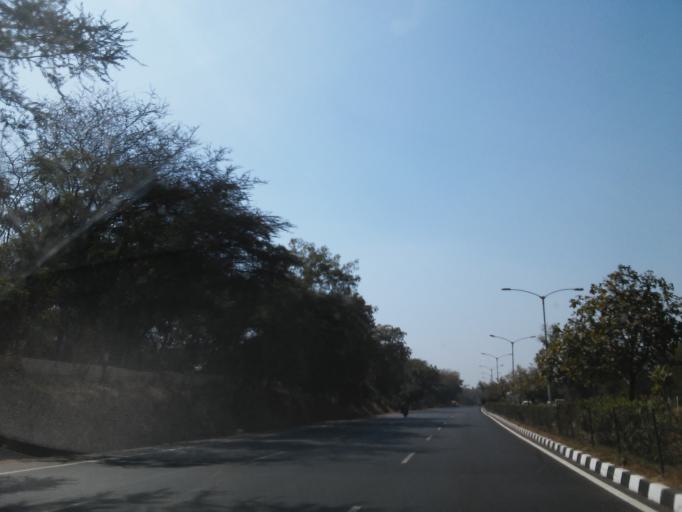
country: IN
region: Gujarat
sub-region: Gandhinagar
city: Ghandinagar
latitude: 23.2008
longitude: 72.6546
